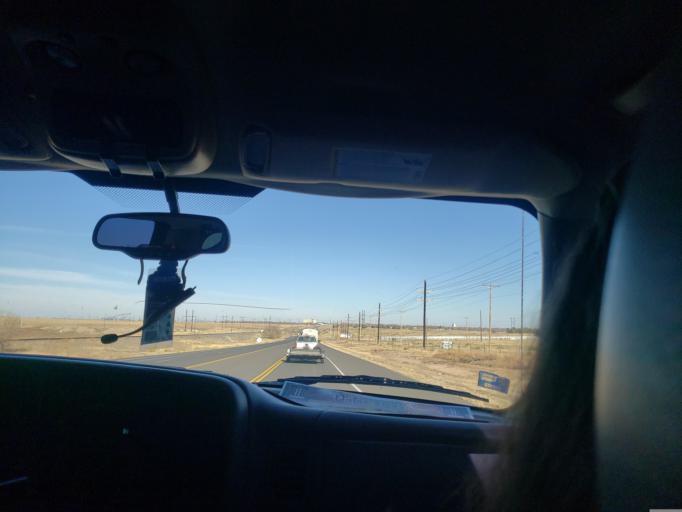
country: US
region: Texas
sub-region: Dallam County
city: Dalhart
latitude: 36.0447
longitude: -102.5518
